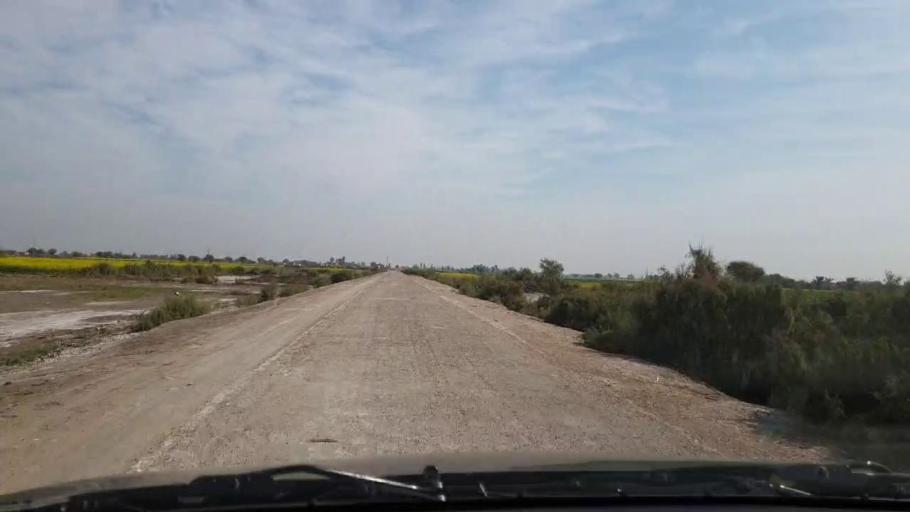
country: PK
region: Sindh
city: Jam Sahib
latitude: 26.2690
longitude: 68.7021
